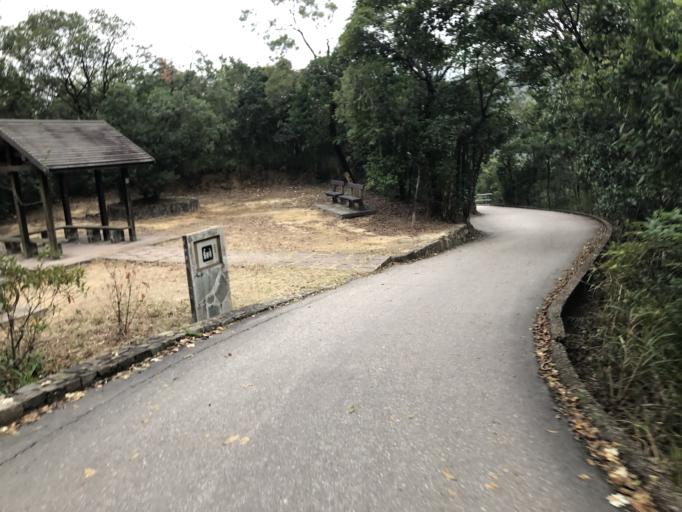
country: HK
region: Wanchai
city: Wan Chai
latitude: 22.2636
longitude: 114.2143
